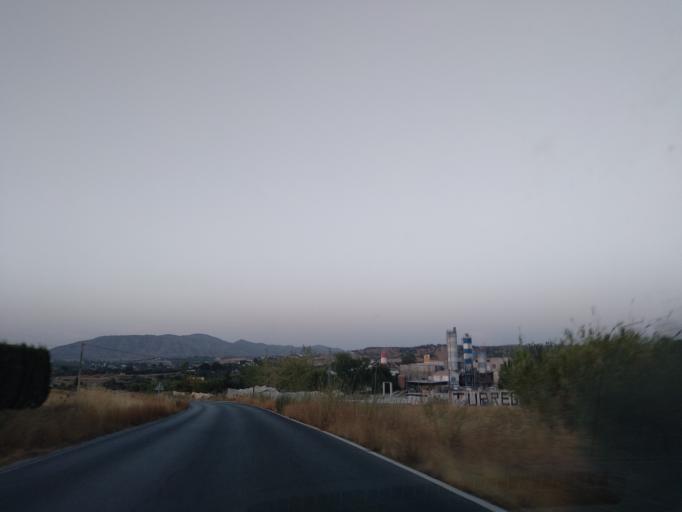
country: ES
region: Andalusia
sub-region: Provincia de Malaga
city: Alhaurin el Grande
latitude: 36.6627
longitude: -4.6710
